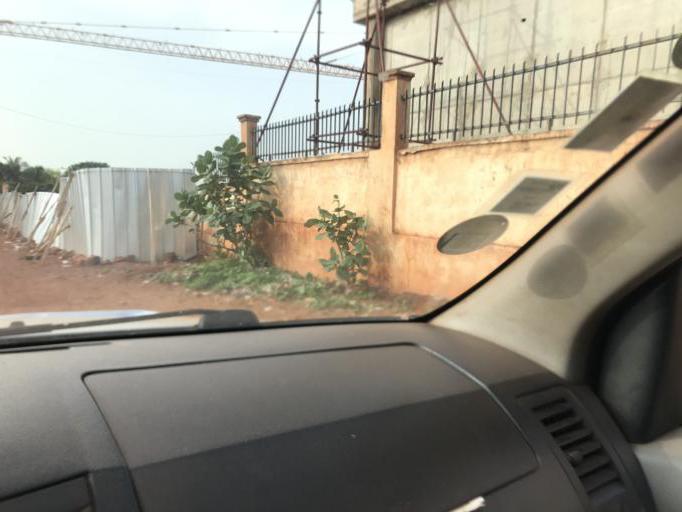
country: ML
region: Bamako
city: Bamako
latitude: 12.5872
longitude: -8.0059
